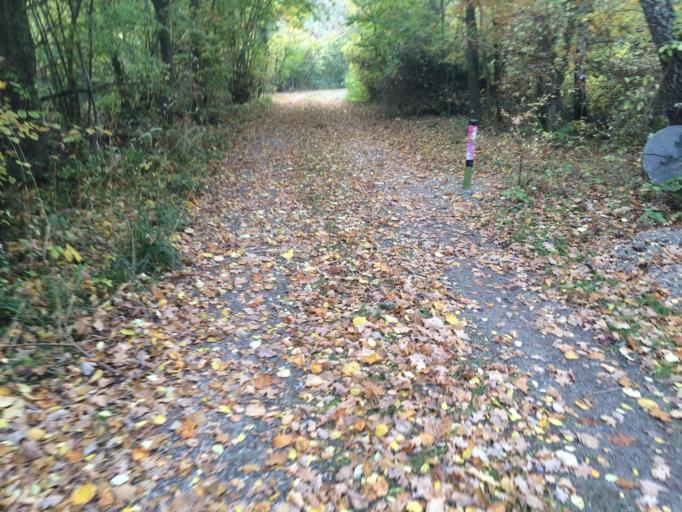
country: DK
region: Zealand
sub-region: Odsherred Kommune
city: Nykobing Sjaelland
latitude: 55.9648
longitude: 11.7515
